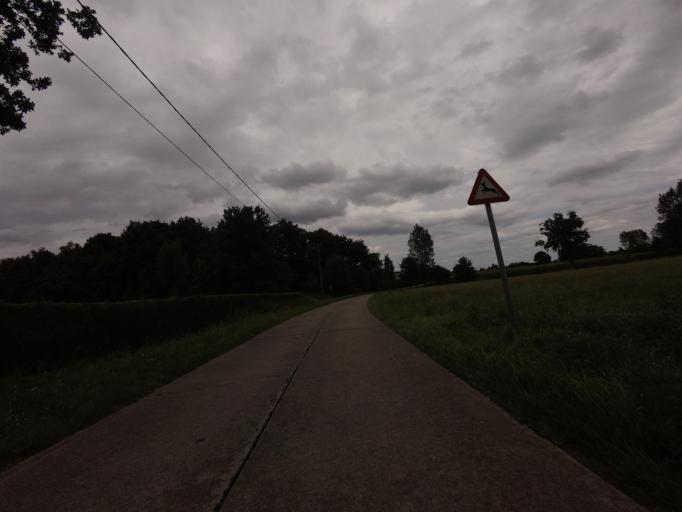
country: BE
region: Flanders
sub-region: Provincie Antwerpen
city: Duffel
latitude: 51.1045
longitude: 4.5284
